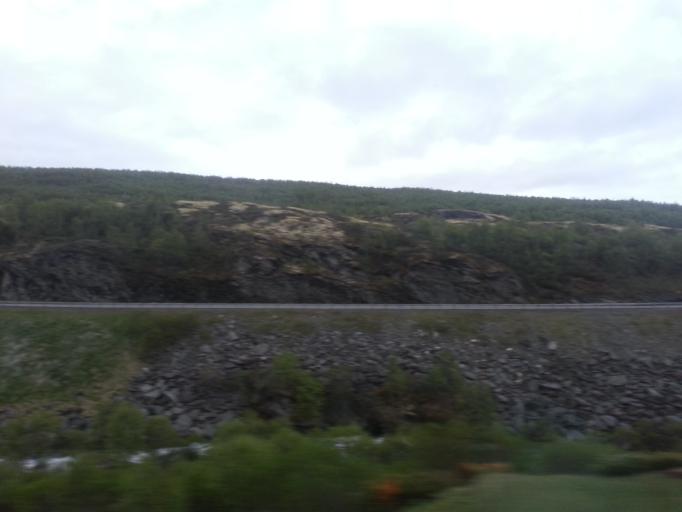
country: NO
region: Sor-Trondelag
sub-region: Oppdal
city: Oppdal
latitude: 62.3014
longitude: 9.6010
